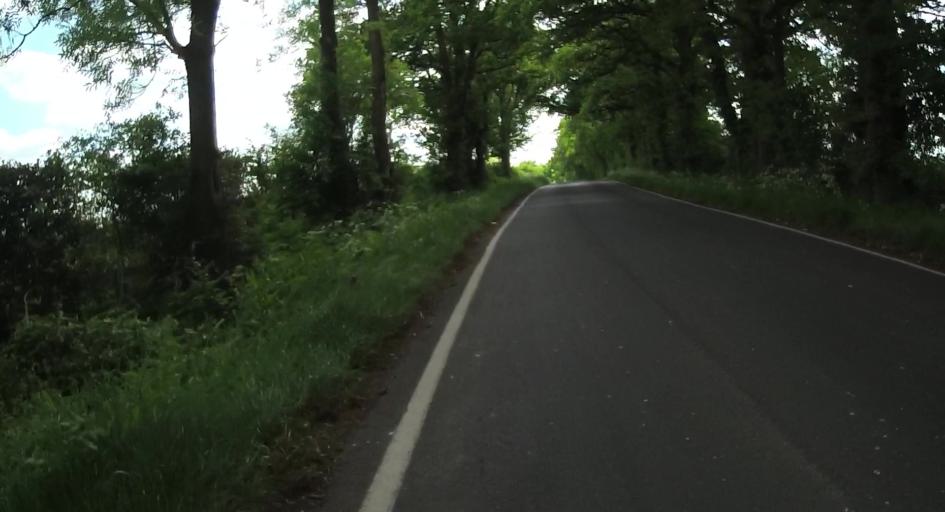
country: GB
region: England
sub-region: Surrey
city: Farnham
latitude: 51.2259
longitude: -0.8373
